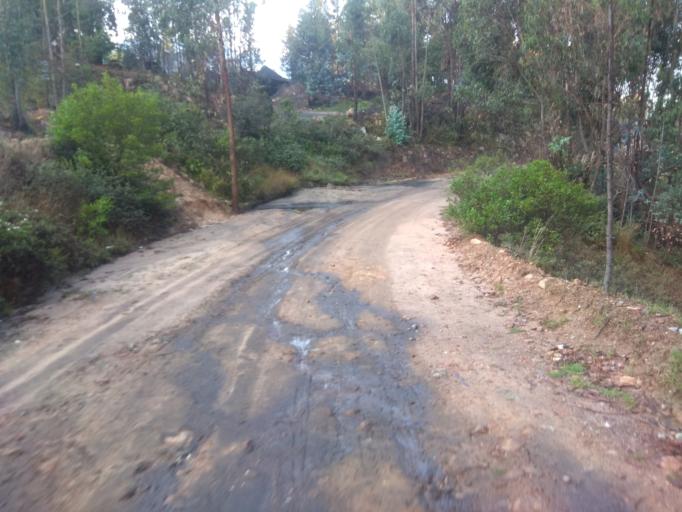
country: CO
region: Boyaca
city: Socha Viejo
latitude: 5.9951
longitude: -72.6993
